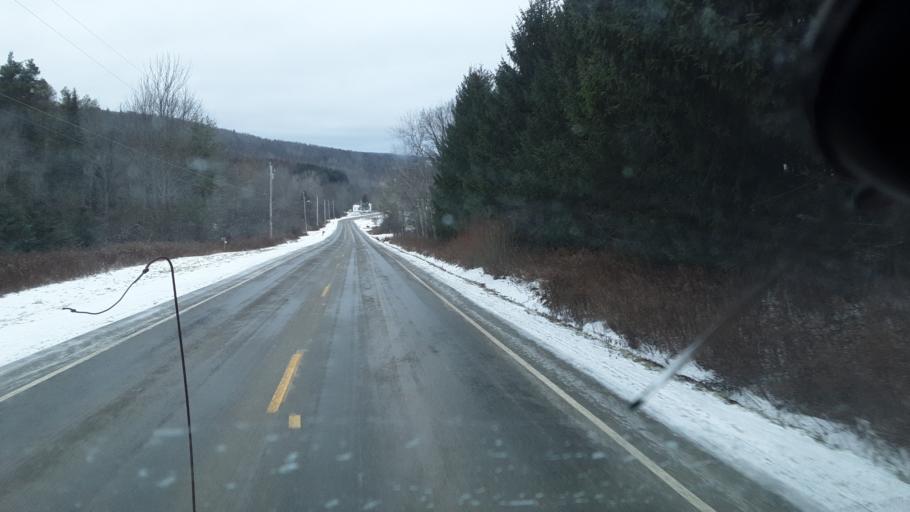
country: US
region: New York
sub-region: Allegany County
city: Friendship
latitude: 42.2537
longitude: -78.1477
